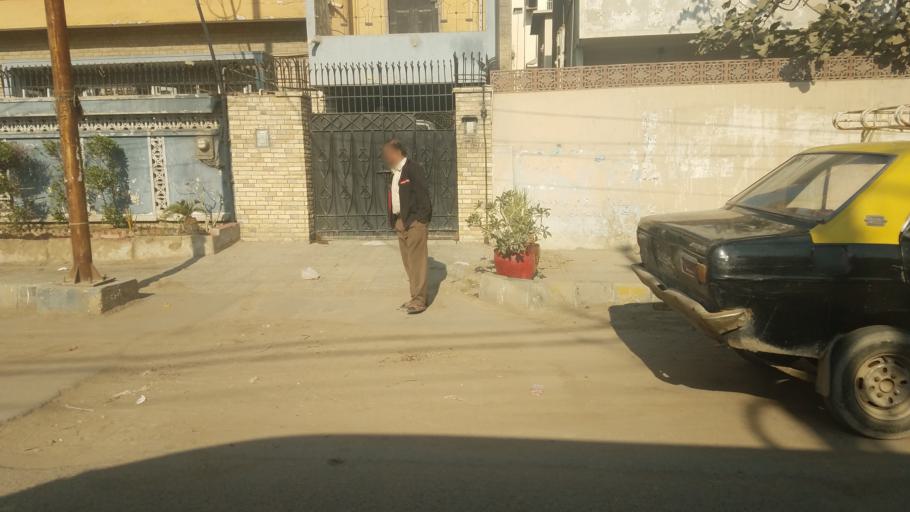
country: PK
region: Sindh
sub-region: Karachi District
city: Karachi
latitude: 24.9384
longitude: 67.0664
